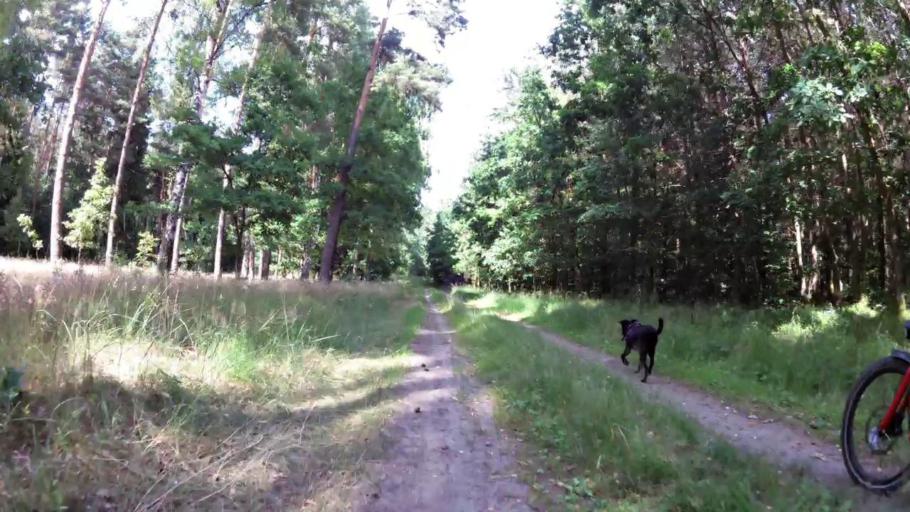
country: PL
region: West Pomeranian Voivodeship
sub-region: Powiat lobeski
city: Lobez
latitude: 53.6121
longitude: 15.6721
